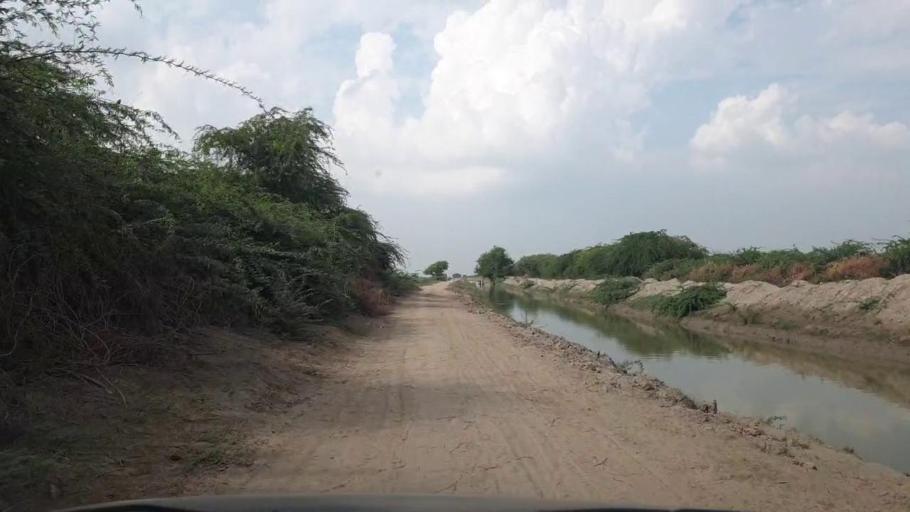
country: PK
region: Sindh
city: Badin
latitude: 24.5656
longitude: 68.6364
